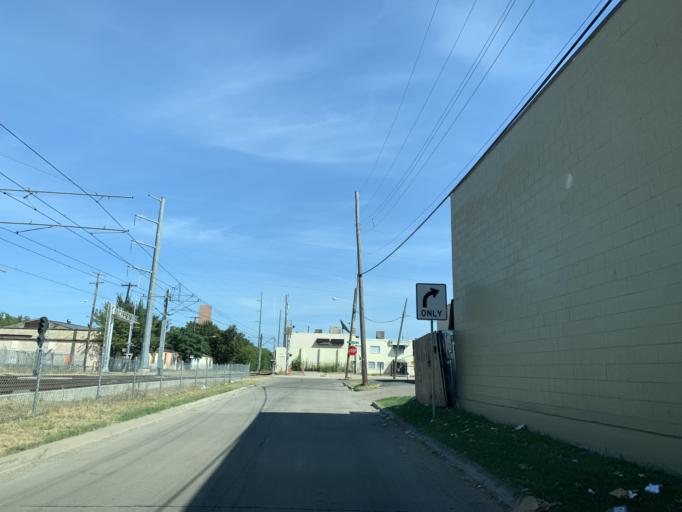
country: US
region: Texas
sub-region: Dallas County
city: Dallas
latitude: 32.7762
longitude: -96.7676
